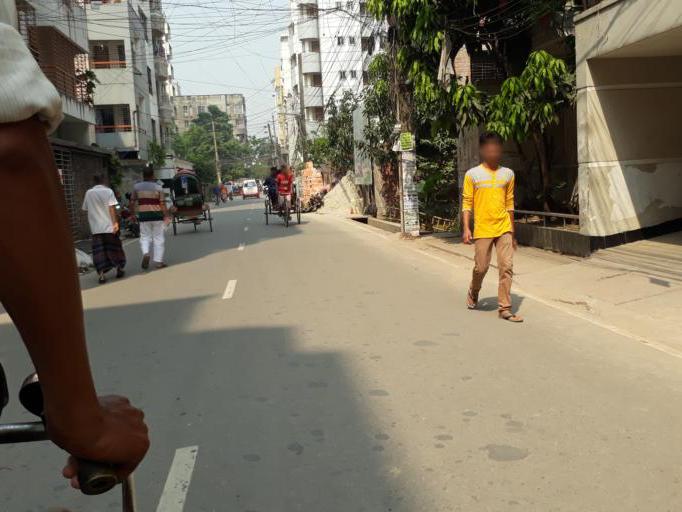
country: BD
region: Dhaka
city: Tungi
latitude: 23.8768
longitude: 90.3855
